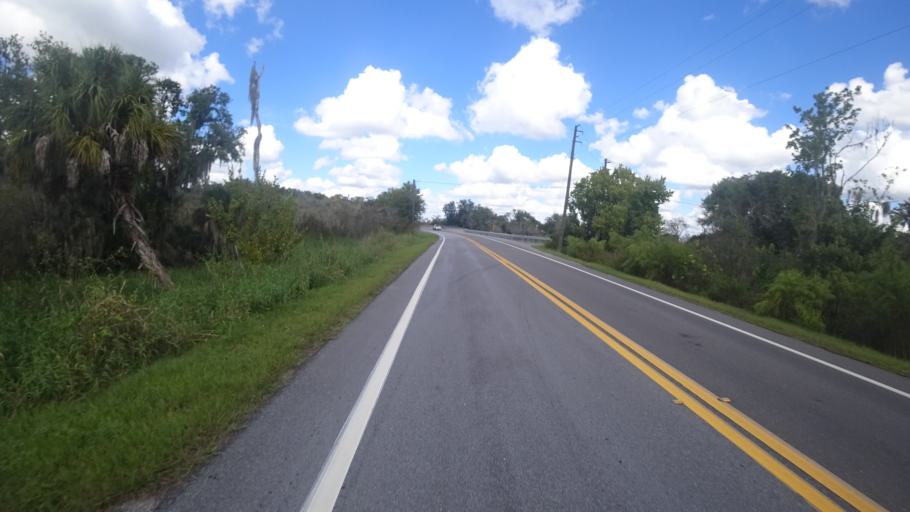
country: US
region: Florida
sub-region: Sarasota County
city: Lake Sarasota
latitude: 27.2990
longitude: -82.2530
